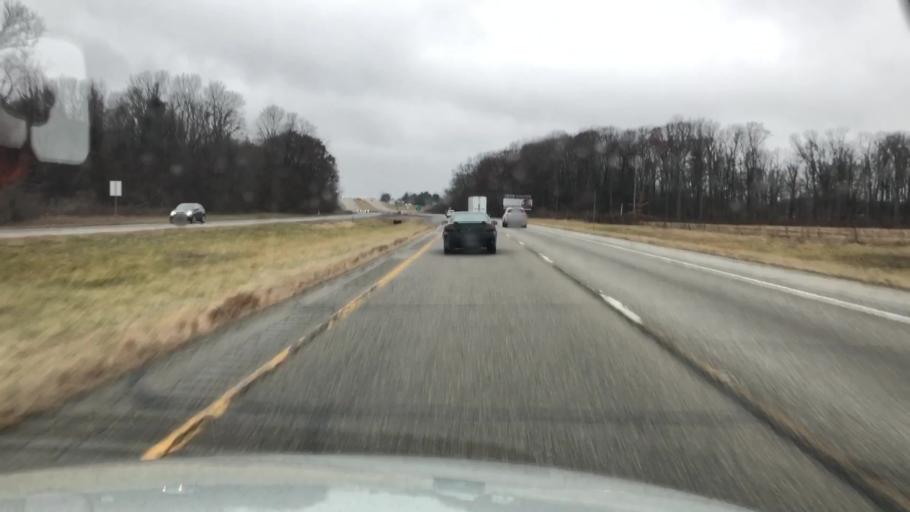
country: US
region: Indiana
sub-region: Marshall County
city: Plymouth
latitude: 41.3624
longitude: -86.3008
